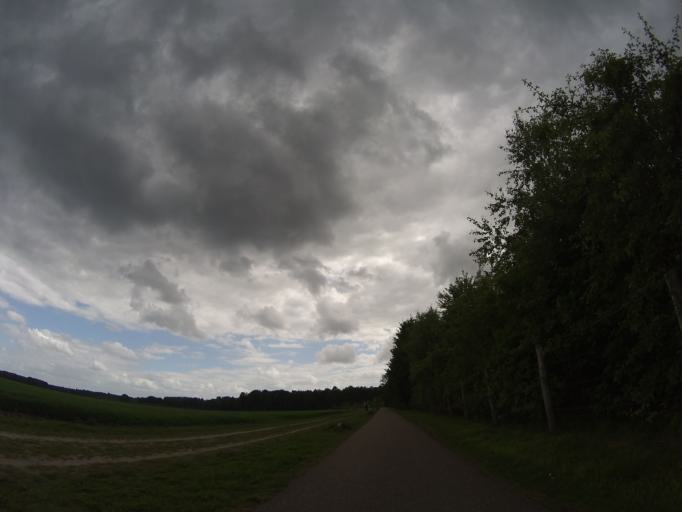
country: NL
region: Drenthe
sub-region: Gemeente Emmen
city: Emmen
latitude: 52.8380
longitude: 6.8727
